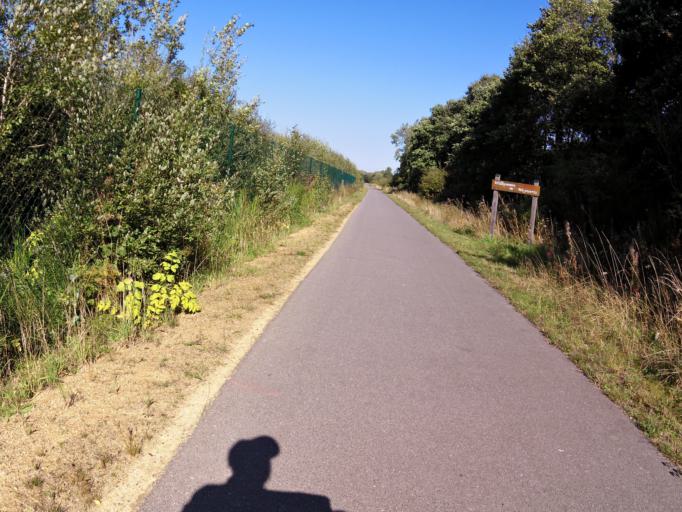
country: BE
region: Wallonia
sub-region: Province de Liege
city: Butgenbach
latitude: 50.4172
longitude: 6.1720
